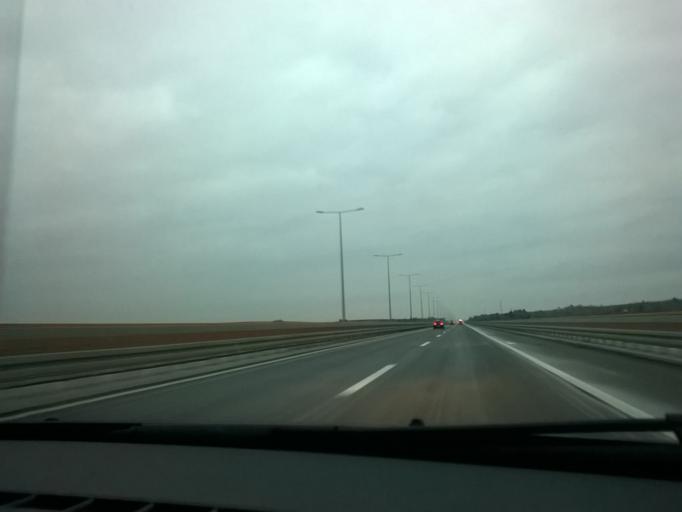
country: RS
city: Beska
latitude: 45.1745
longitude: 20.0789
